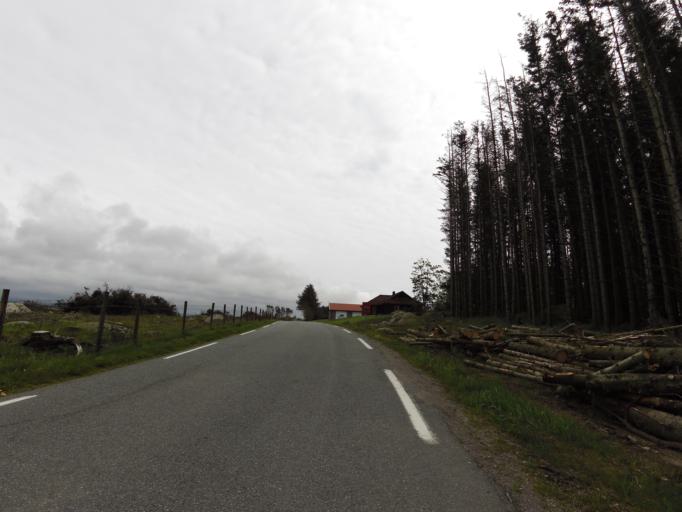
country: NO
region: Rogaland
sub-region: Ha
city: Naerbo
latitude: 58.6603
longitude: 5.5597
